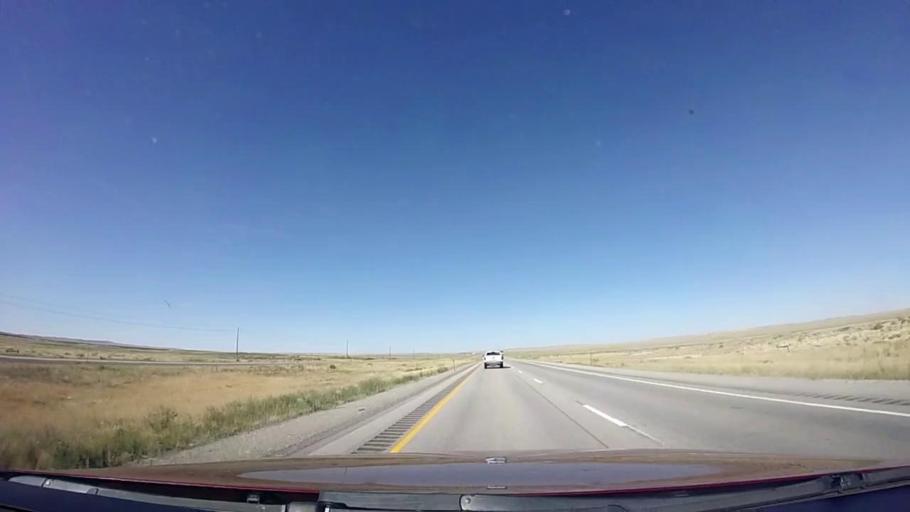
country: US
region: Wyoming
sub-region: Carbon County
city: Rawlins
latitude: 41.7804
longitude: -107.4348
